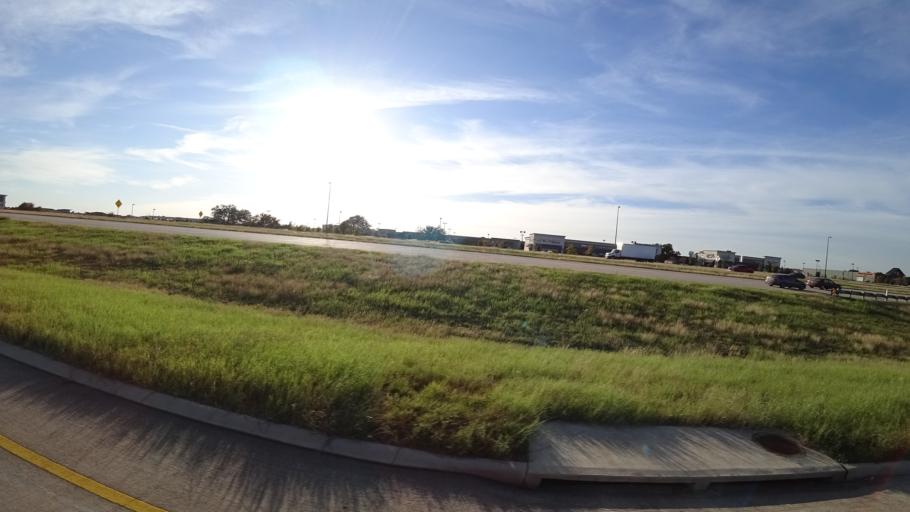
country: US
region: Texas
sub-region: Williamson County
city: Cedar Park
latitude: 30.5280
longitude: -97.8164
